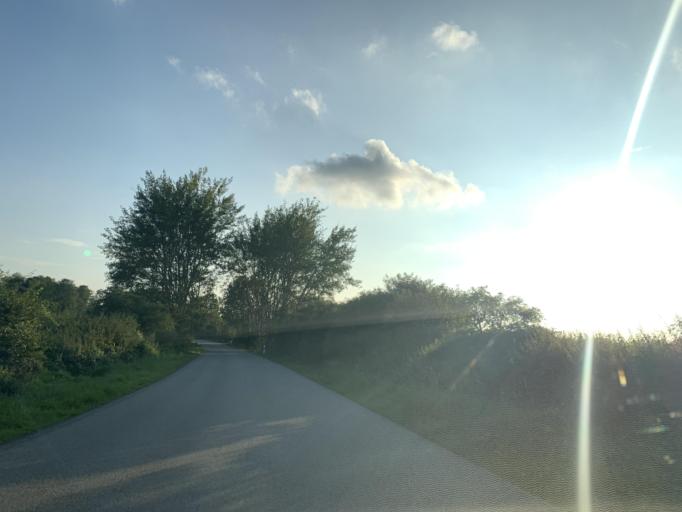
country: DE
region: Mecklenburg-Vorpommern
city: Loitz
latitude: 53.3612
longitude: 13.4375
